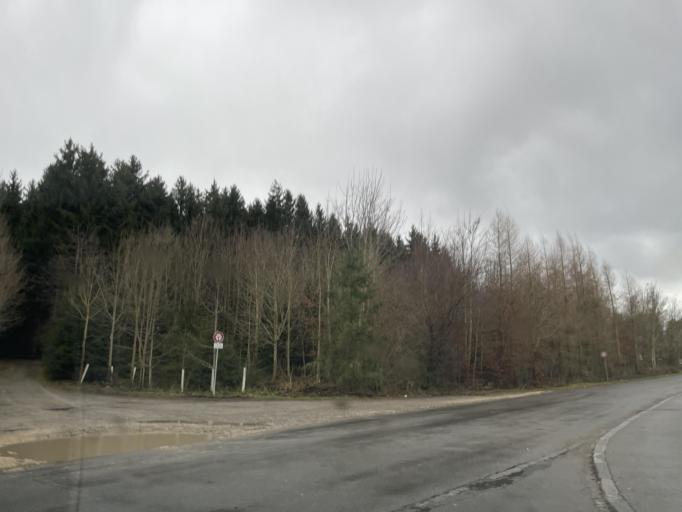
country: CH
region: Bern
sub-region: Bern-Mittelland District
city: Zollikofen
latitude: 47.0108
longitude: 7.4616
